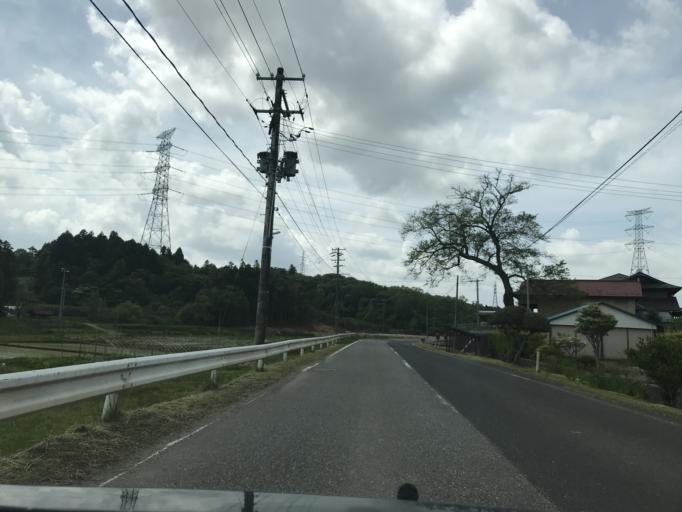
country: JP
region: Iwate
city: Ichinoseki
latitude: 38.8129
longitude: 141.0209
